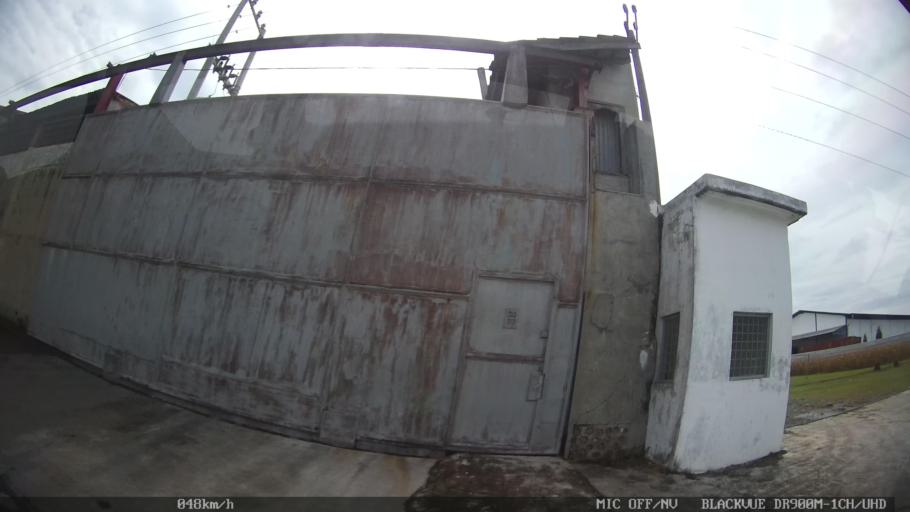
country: ID
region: North Sumatra
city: Sunggal
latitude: 3.5935
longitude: 98.5832
